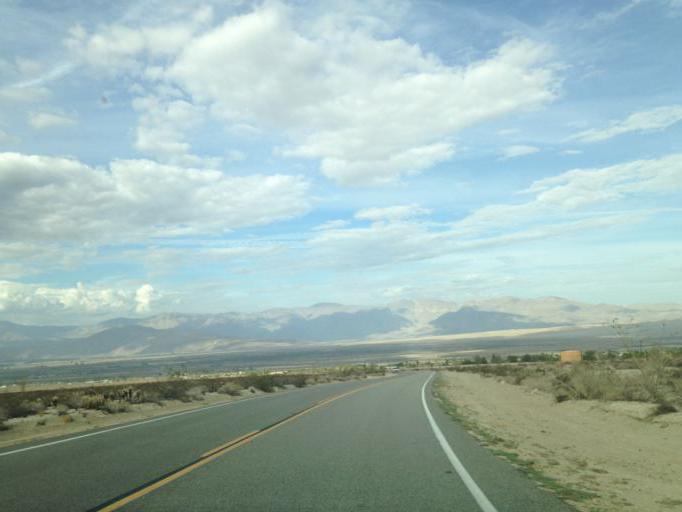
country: US
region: California
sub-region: San Diego County
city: Borrego Springs
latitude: 33.1814
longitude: -116.3323
